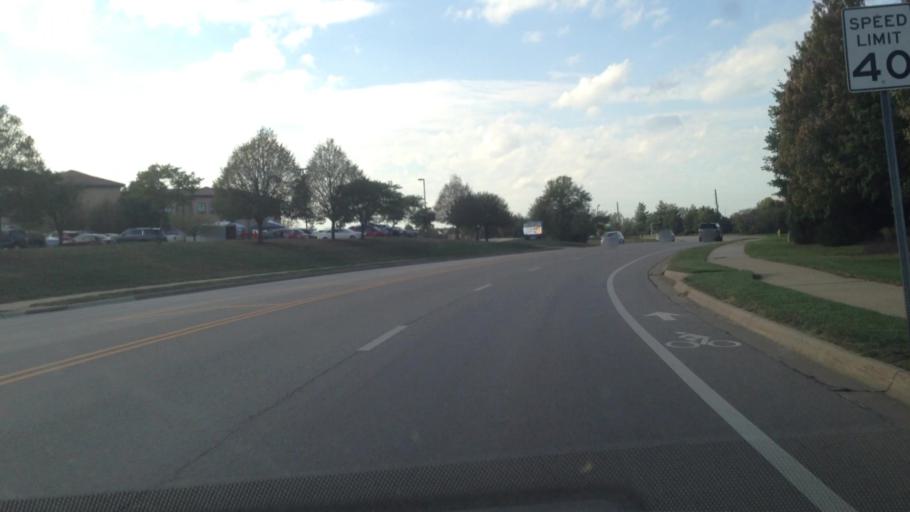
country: US
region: Kansas
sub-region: Douglas County
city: Lawrence
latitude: 38.9574
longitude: -95.3220
